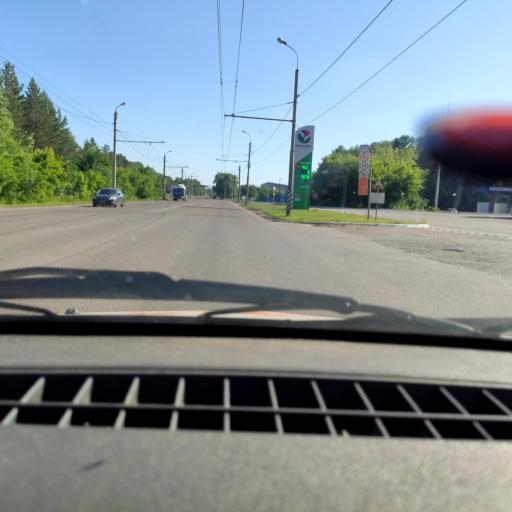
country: RU
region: Bashkortostan
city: Sterlitamak
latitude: 53.6565
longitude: 55.9211
